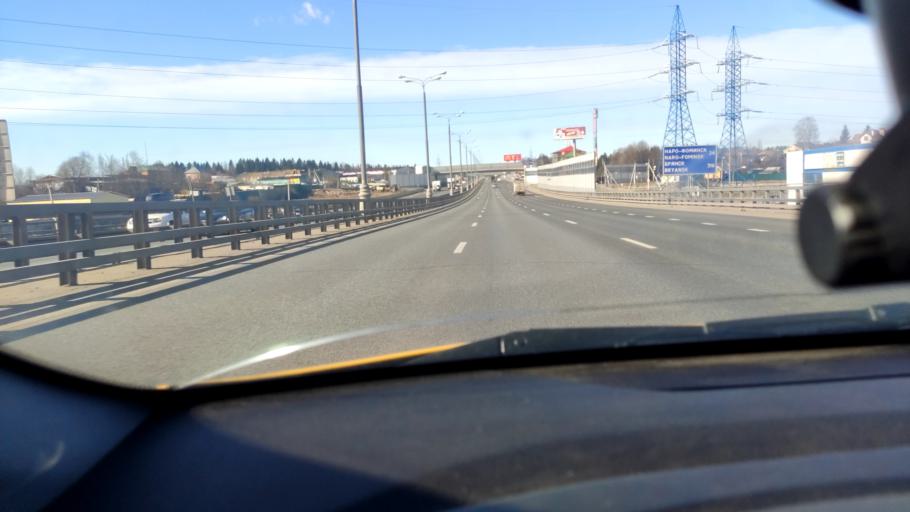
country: RU
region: Moskovskaya
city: Selyatino
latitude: 55.5240
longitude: 37.0206
